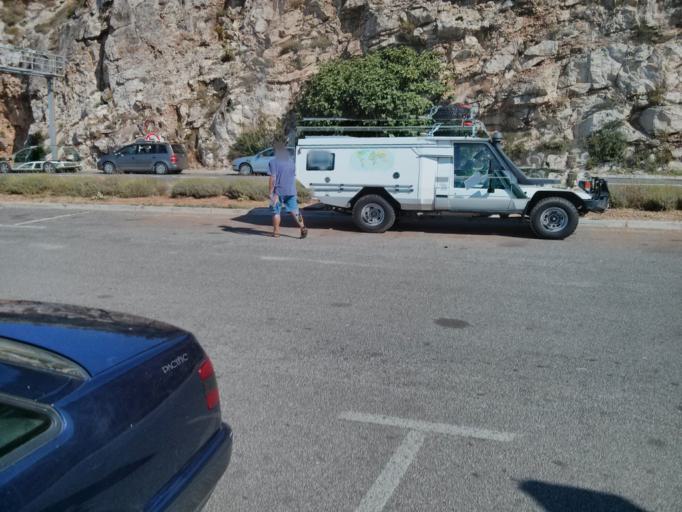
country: HR
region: Dubrovacko-Neretvanska
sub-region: Grad Dubrovnik
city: Mokosica
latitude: 42.6702
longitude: 18.0763
